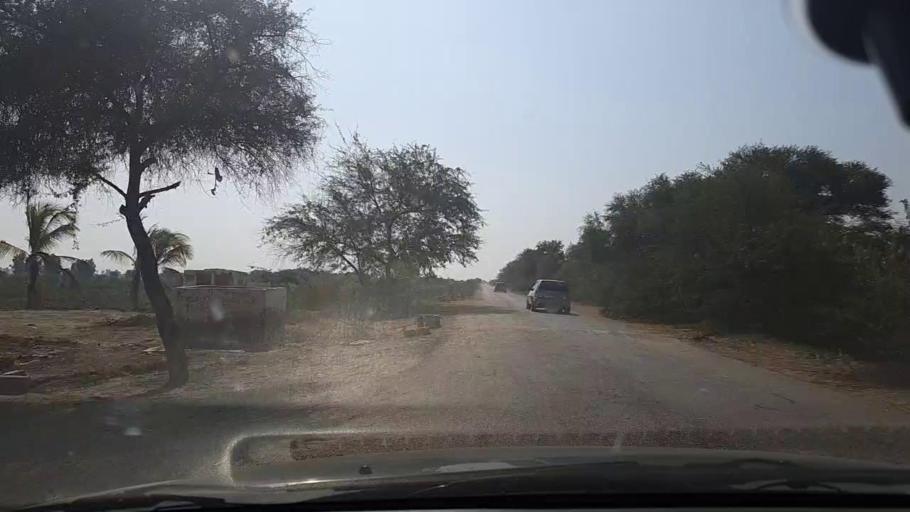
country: PK
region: Sindh
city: Chuhar Jamali
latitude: 24.5198
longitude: 67.8787
